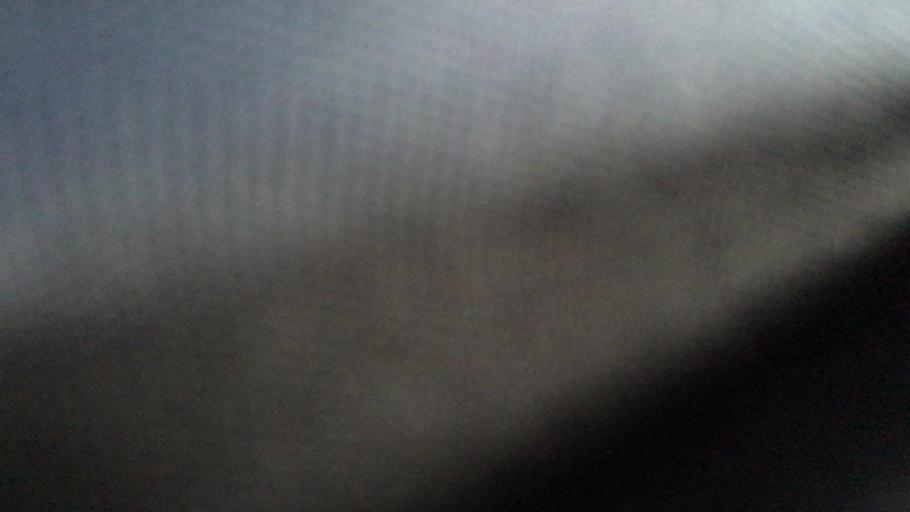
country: US
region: Maryland
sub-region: Somerset County
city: Princess Anne
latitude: 38.1440
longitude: -75.6987
